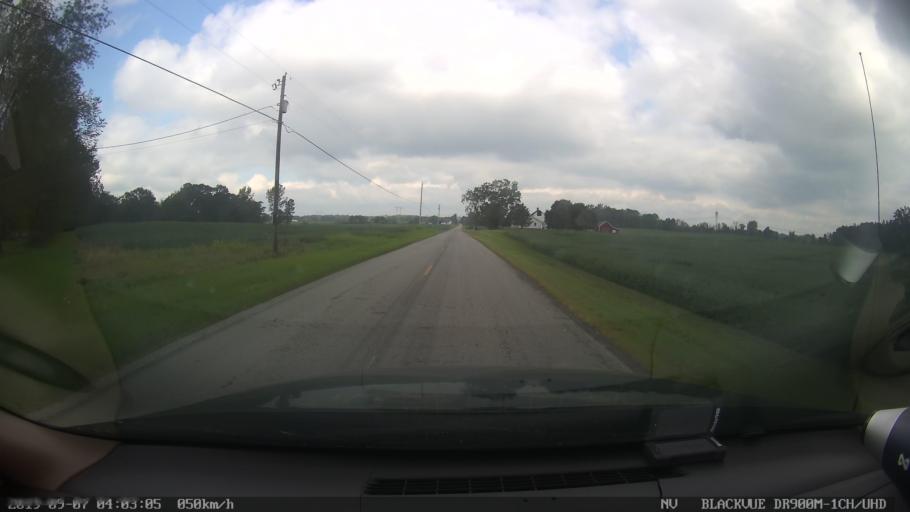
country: US
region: Ohio
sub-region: Licking County
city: Johnstown
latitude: 40.1825
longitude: -82.5889
